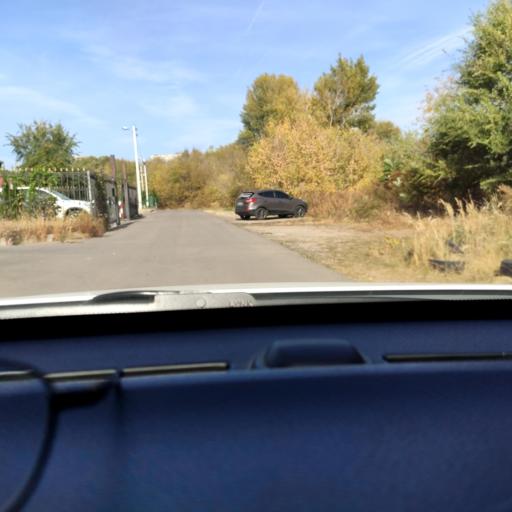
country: RU
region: Voronezj
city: Voronezh
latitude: 51.6463
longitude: 39.2098
